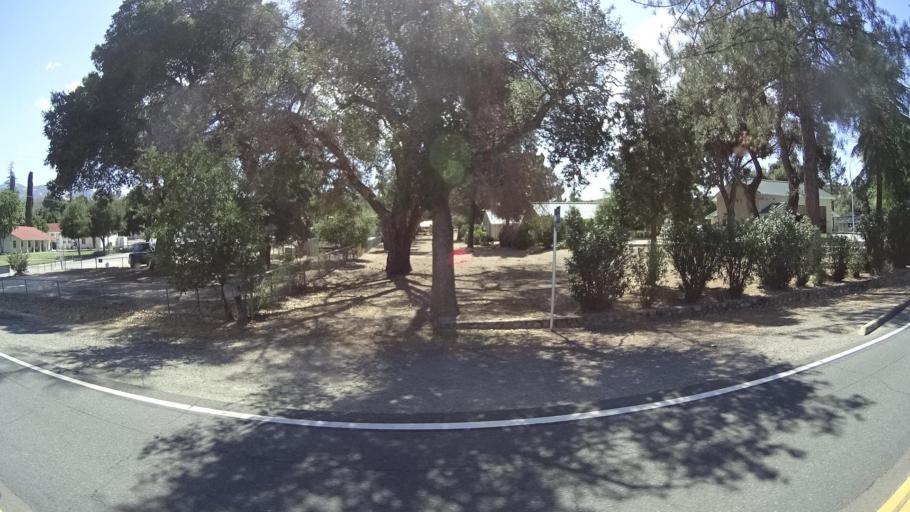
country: US
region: California
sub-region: San Diego County
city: Julian
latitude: 33.2741
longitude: -116.6443
